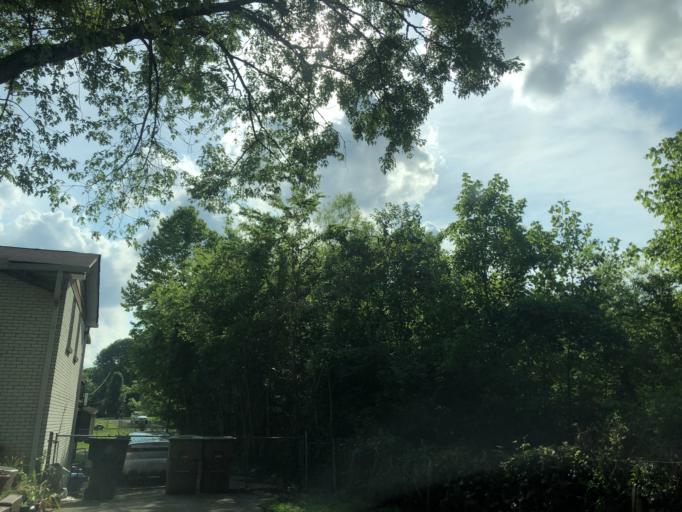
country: US
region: Tennessee
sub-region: Davidson County
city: Nashville
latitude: 36.2293
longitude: -86.8267
